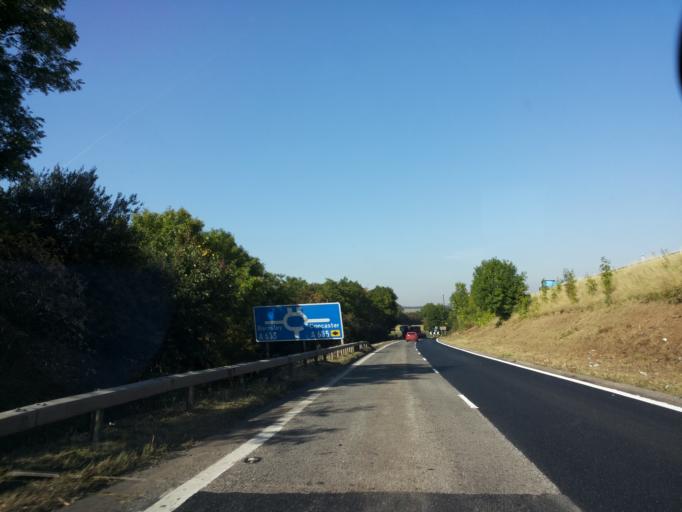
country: GB
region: England
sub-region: Doncaster
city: Marr
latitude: 53.5399
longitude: -1.2050
